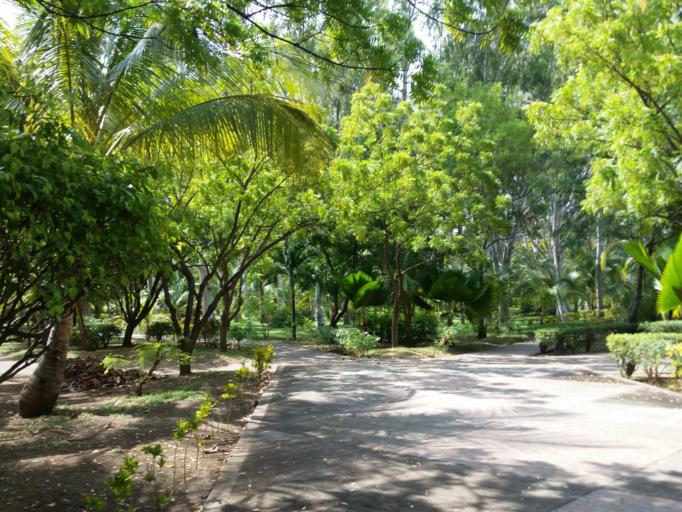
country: NI
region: Managua
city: Masachapa
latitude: 11.8089
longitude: -86.5220
